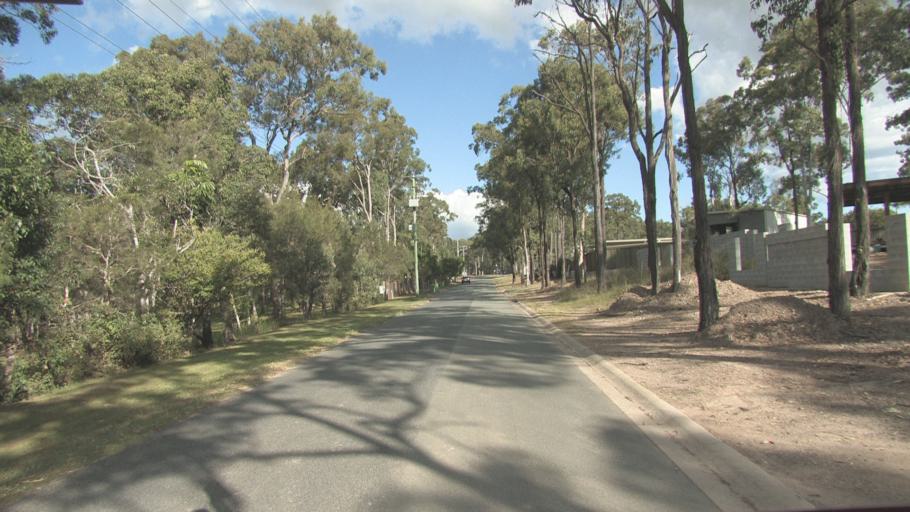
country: AU
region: Queensland
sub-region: Logan
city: Beenleigh
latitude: -27.6663
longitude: 153.2216
